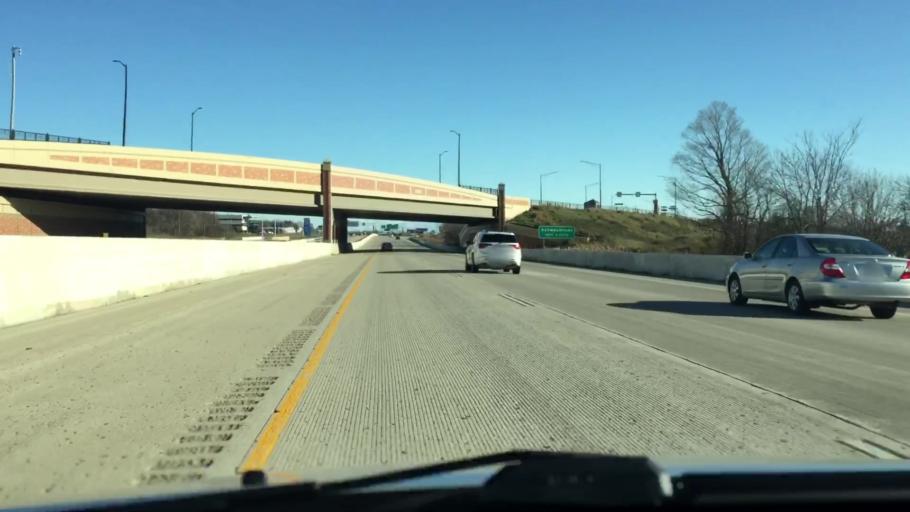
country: US
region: Wisconsin
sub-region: Brown County
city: De Pere
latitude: 44.4299
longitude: -88.1131
